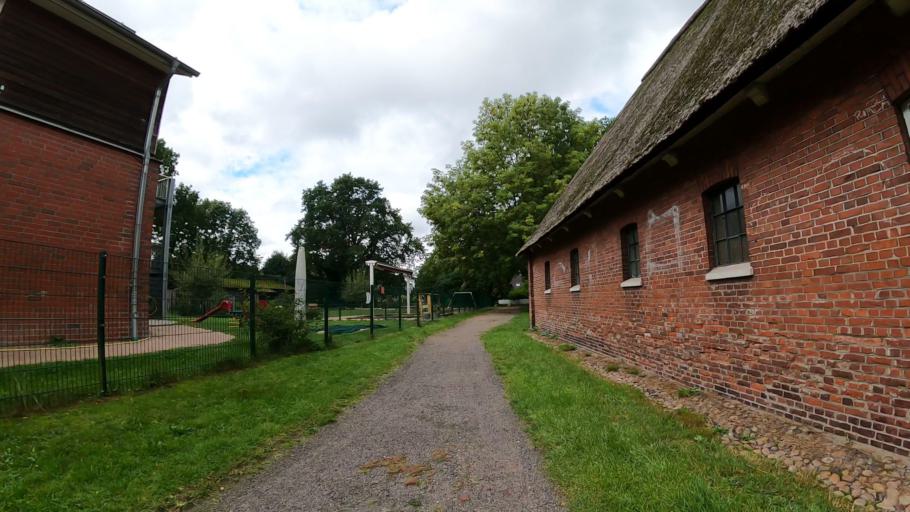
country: DE
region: Lower Saxony
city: Neu Wulmstorf
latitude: 53.4797
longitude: 9.8624
